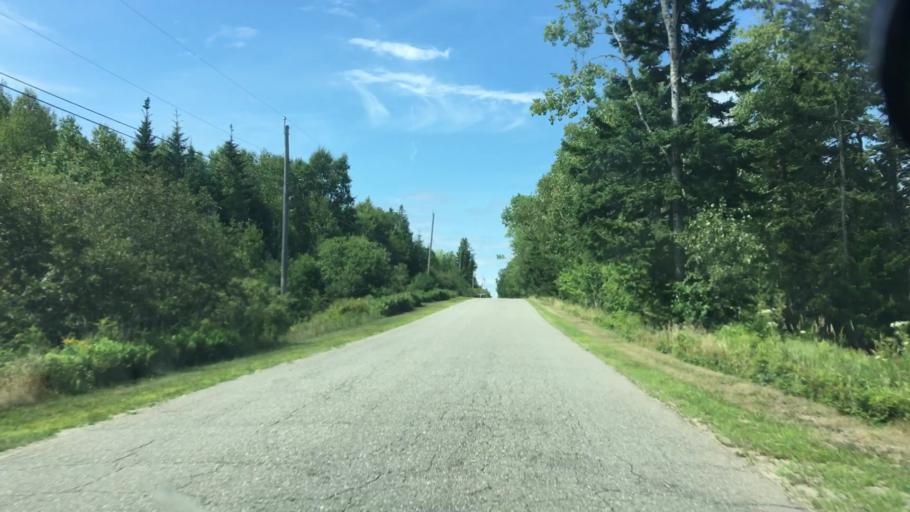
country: US
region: Maine
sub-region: Washington County
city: Eastport
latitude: 44.9310
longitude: -67.0415
